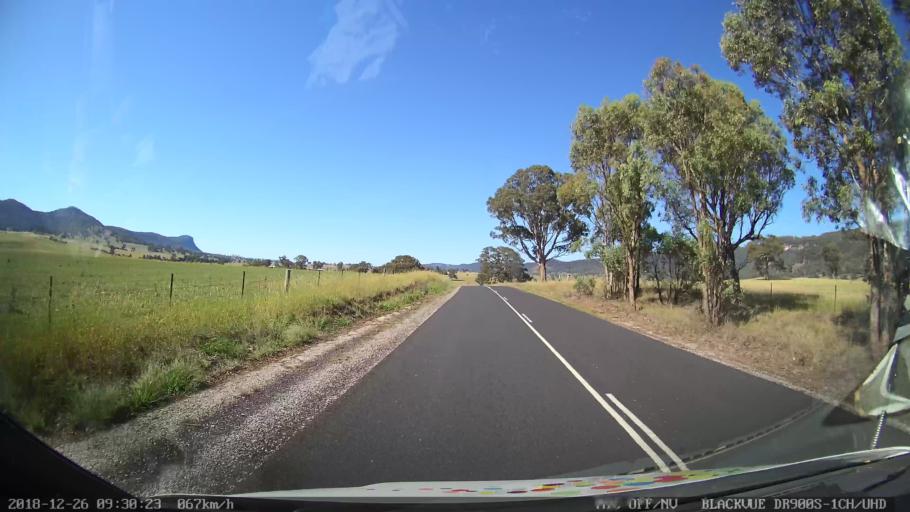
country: AU
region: New South Wales
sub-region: Mid-Western Regional
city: Kandos
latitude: -32.8623
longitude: 150.0293
